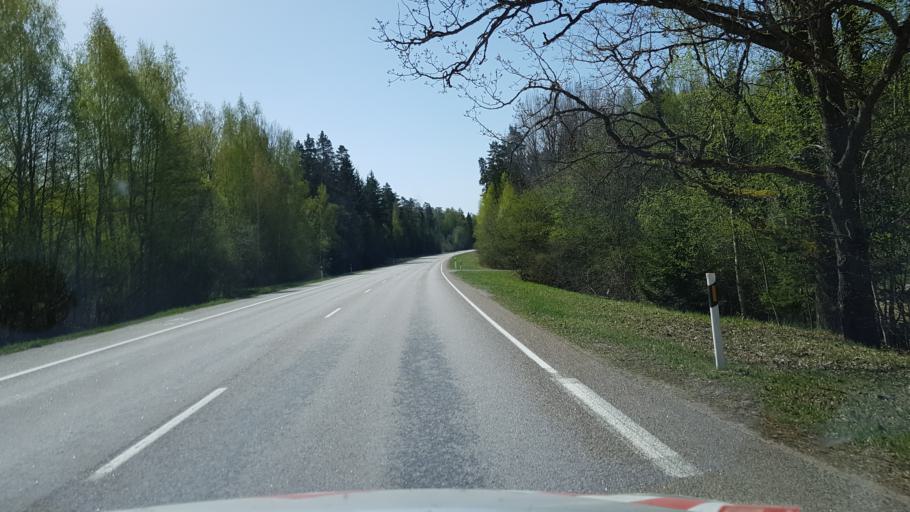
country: EE
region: Valgamaa
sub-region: Valga linn
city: Valga
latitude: 57.8364
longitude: 26.0593
